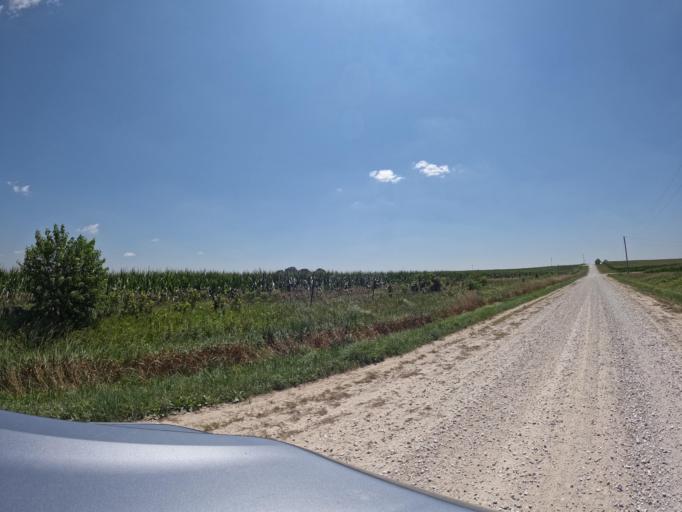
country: US
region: Iowa
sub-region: Keokuk County
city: Sigourney
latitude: 41.2895
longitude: -92.2187
